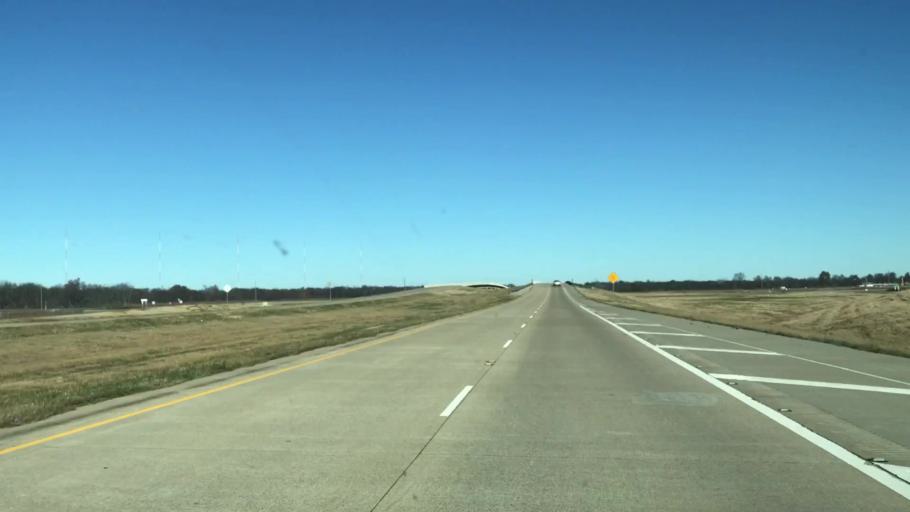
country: US
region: Louisiana
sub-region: Caddo Parish
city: Blanchard
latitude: 32.6714
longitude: -93.8486
